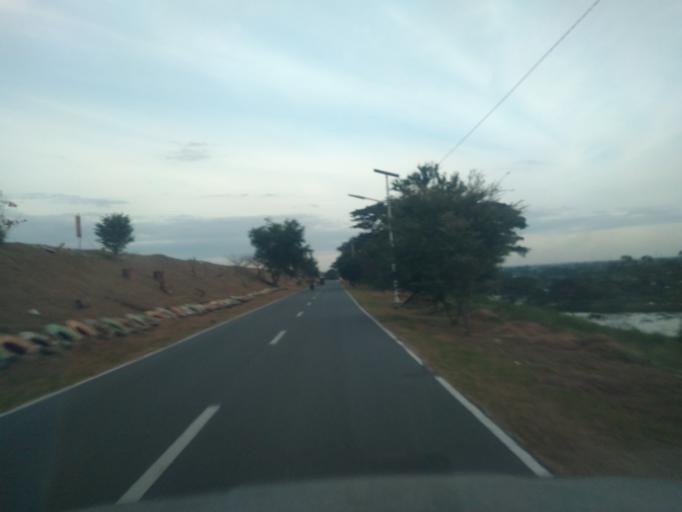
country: PH
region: Central Luzon
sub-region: Province of Pampanga
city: Santa Rita
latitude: 15.0180
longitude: 120.6082
